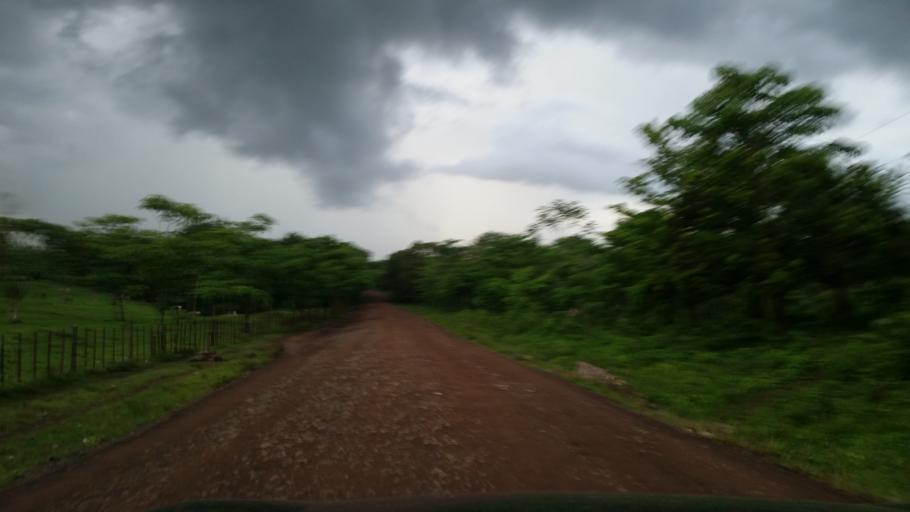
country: NI
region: Atlantico Norte (RAAN)
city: Siuna
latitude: 13.3888
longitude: -84.8569
